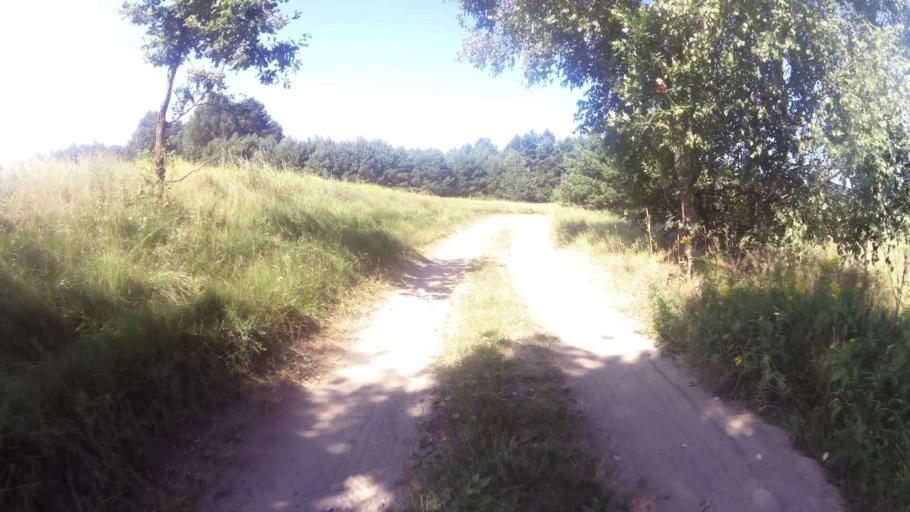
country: PL
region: West Pomeranian Voivodeship
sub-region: Powiat stargardzki
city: Insko
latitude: 53.4402
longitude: 15.6260
